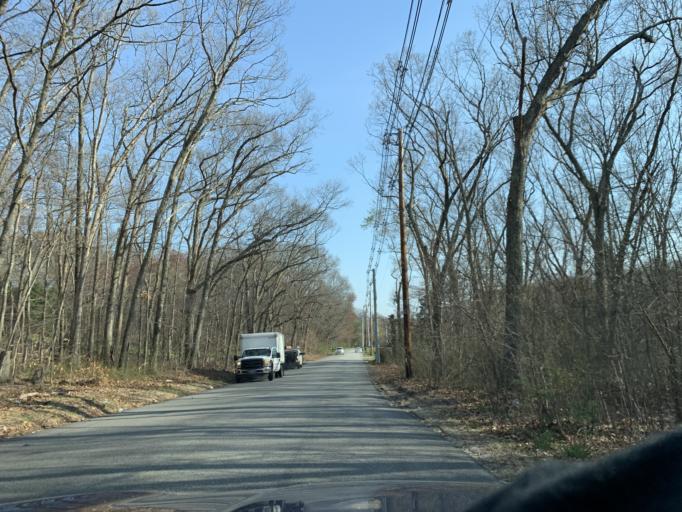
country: US
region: Rhode Island
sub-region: Kent County
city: West Warwick
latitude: 41.7364
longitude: -71.5342
